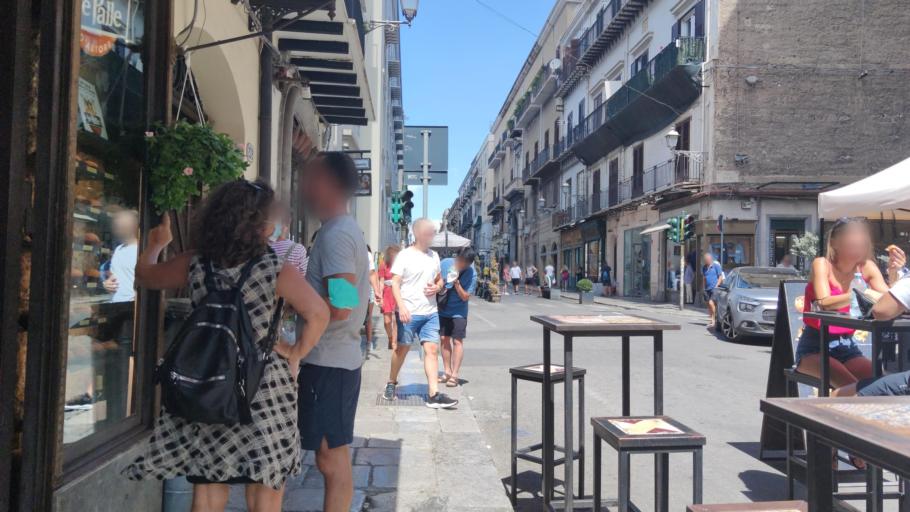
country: IT
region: Sicily
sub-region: Palermo
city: Palermo
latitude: 38.1177
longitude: 13.3601
